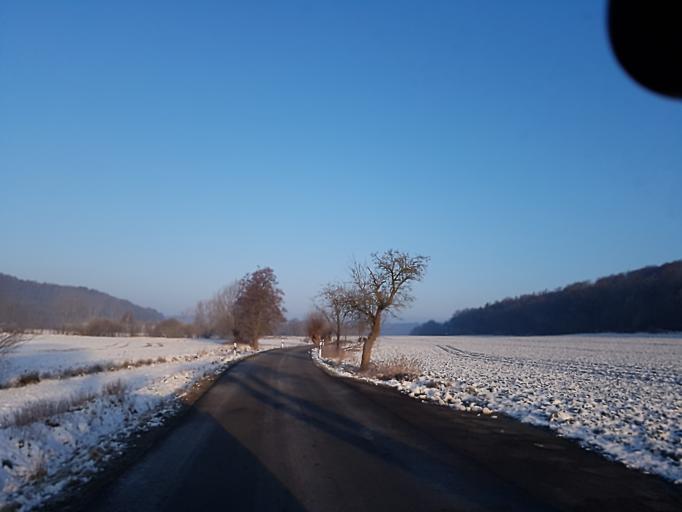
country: DE
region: Saxony
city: Grossweitzschen
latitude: 51.1432
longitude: 13.0165
